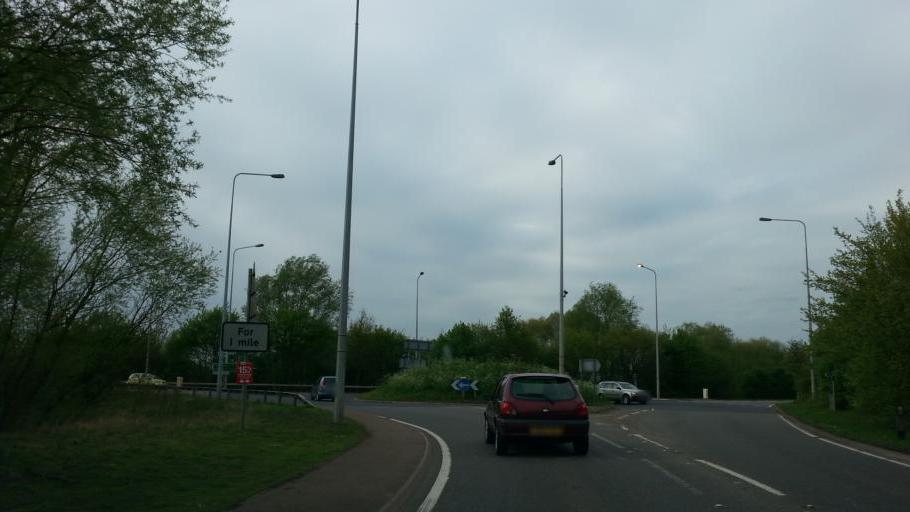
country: GB
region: England
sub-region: Cambridgeshire
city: March
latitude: 52.6062
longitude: 0.0635
